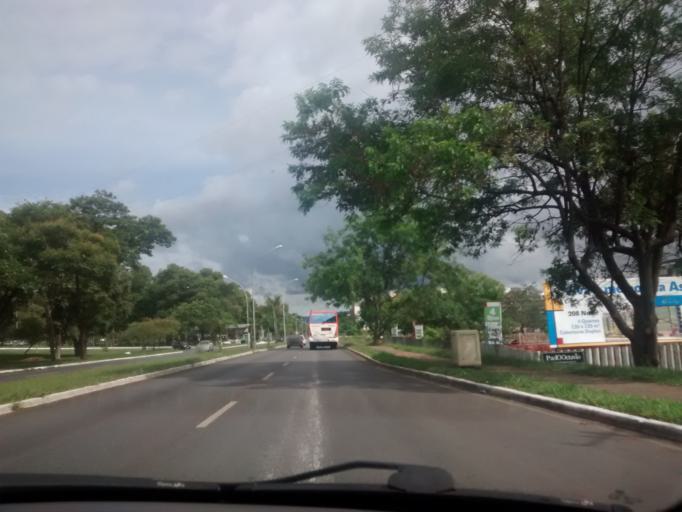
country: BR
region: Federal District
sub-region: Brasilia
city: Brasilia
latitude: -15.7636
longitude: -47.8829
